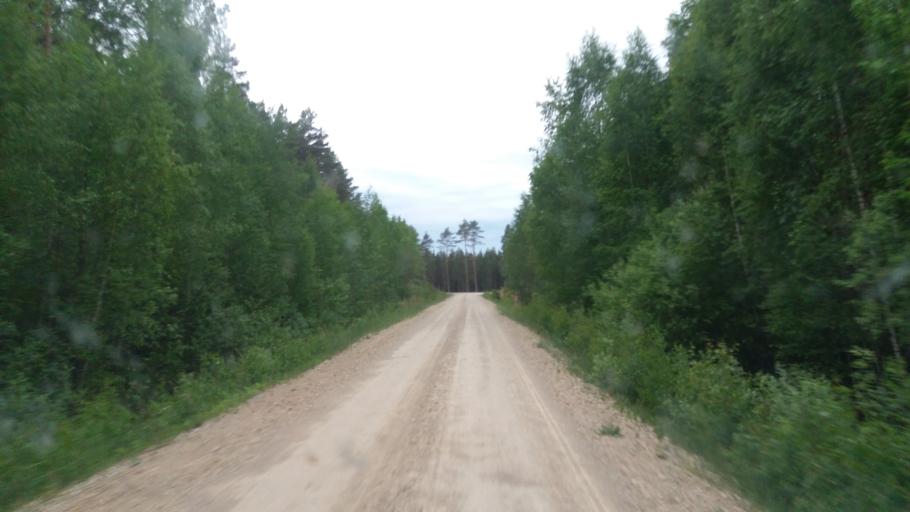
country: LV
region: Kuldigas Rajons
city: Kuldiga
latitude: 57.1530
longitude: 22.1191
